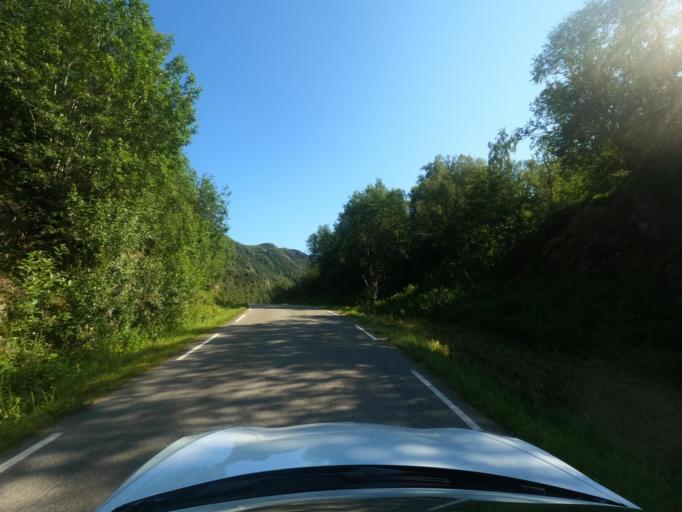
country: NO
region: Nordland
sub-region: Hadsel
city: Stokmarknes
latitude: 68.3048
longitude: 15.0750
